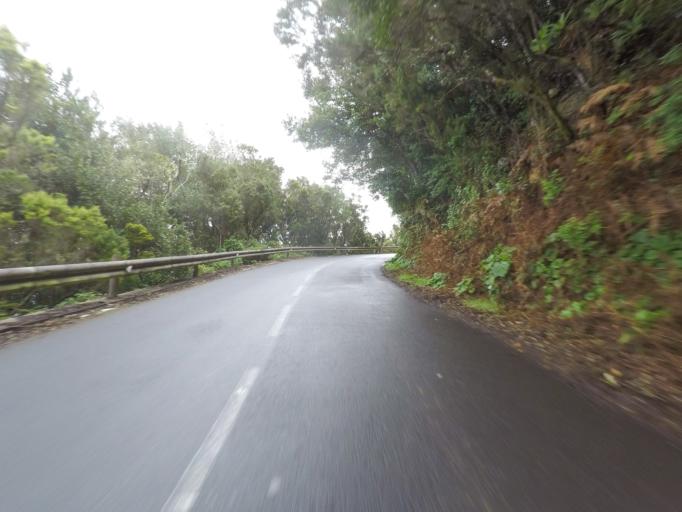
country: ES
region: Canary Islands
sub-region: Provincia de Santa Cruz de Tenerife
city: Vallehermosa
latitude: 28.1622
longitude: -17.2941
